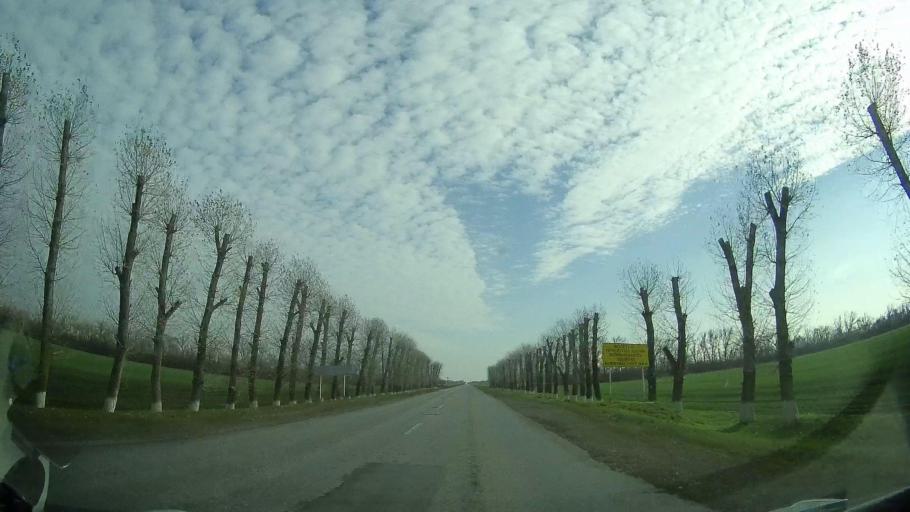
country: RU
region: Rostov
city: Tselina
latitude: 46.5277
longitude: 41.0635
